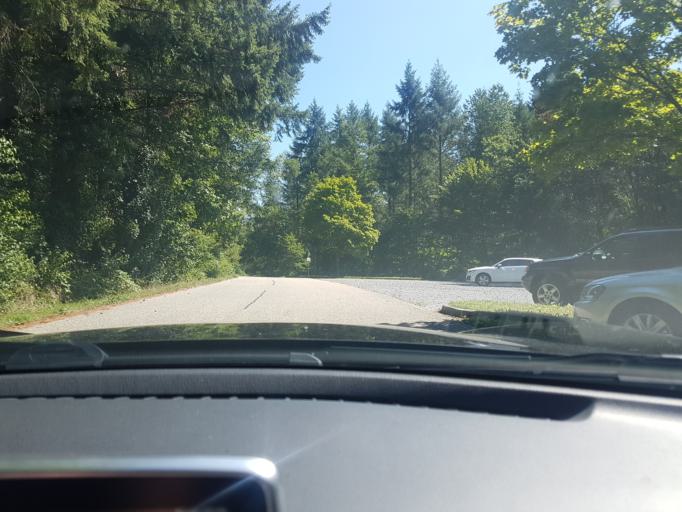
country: DE
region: Baden-Wuerttemberg
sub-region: Regierungsbezirk Stuttgart
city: Gundelsheim
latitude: 49.2772
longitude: 9.1324
